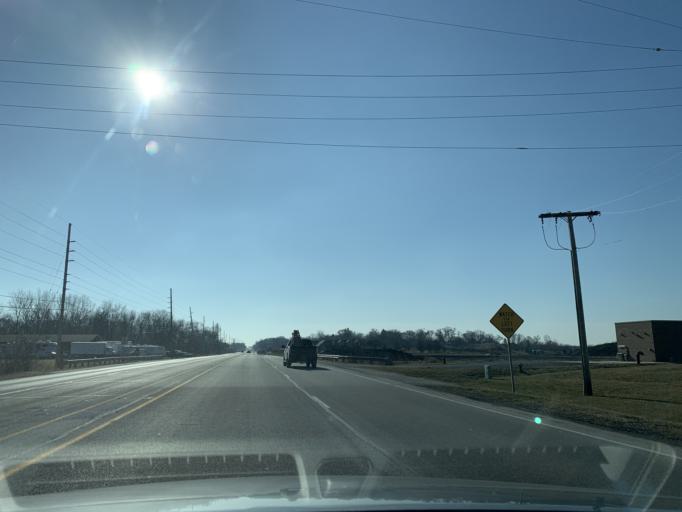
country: US
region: Indiana
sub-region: Lake County
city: Saint John
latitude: 41.4293
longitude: -87.4701
